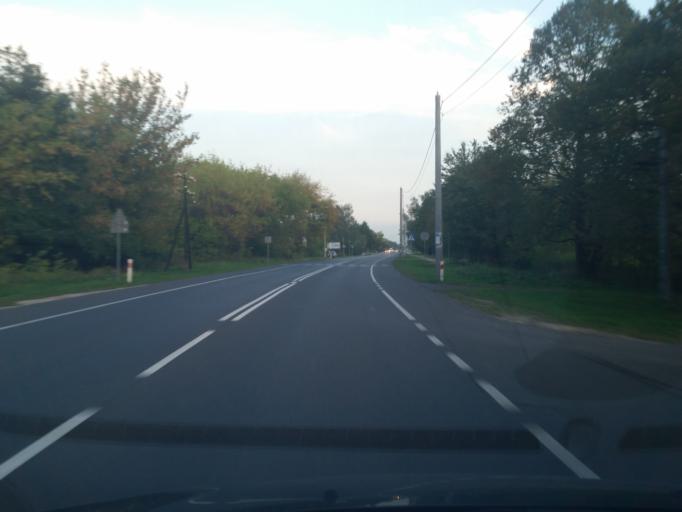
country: PL
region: Masovian Voivodeship
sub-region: Powiat legionowski
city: Jablonna
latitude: 52.3882
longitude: 20.8914
